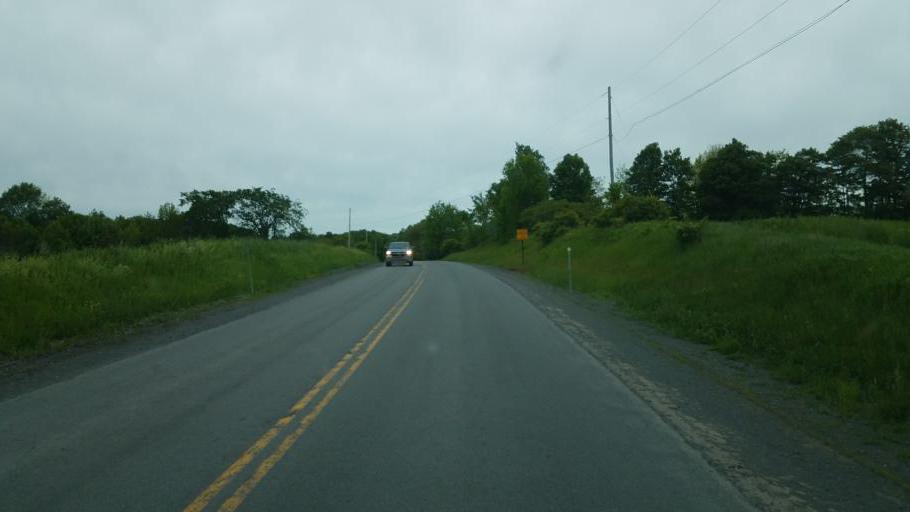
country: US
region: New York
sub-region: Oneida County
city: Chadwicks
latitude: 42.9423
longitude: -75.2212
